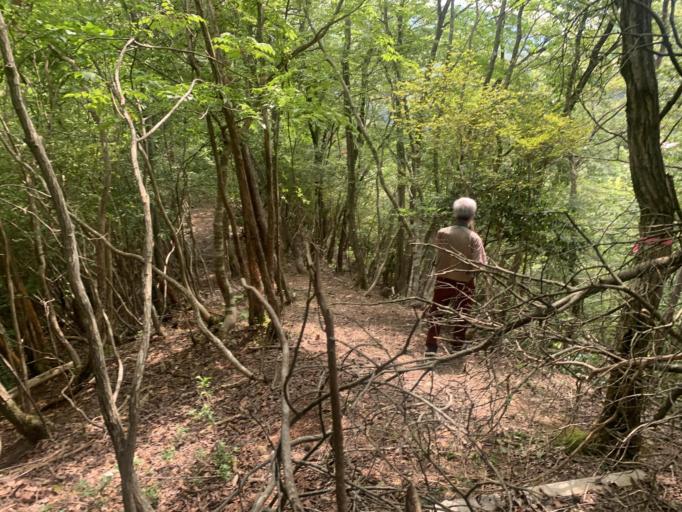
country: JP
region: Kyoto
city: Miyazu
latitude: 35.4486
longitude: 135.1632
